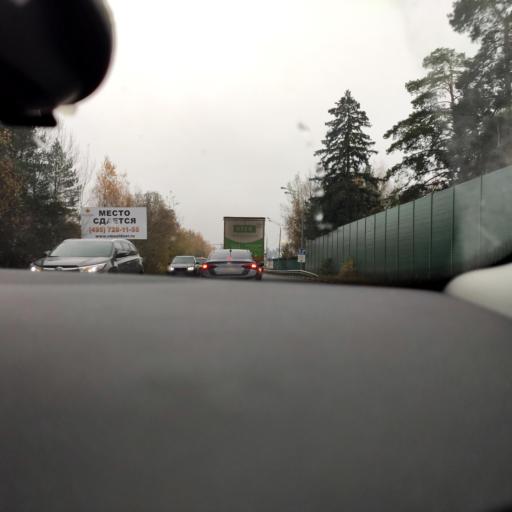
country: RU
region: Moskovskaya
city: Pavlovskaya Sloboda
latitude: 55.8043
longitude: 37.1269
